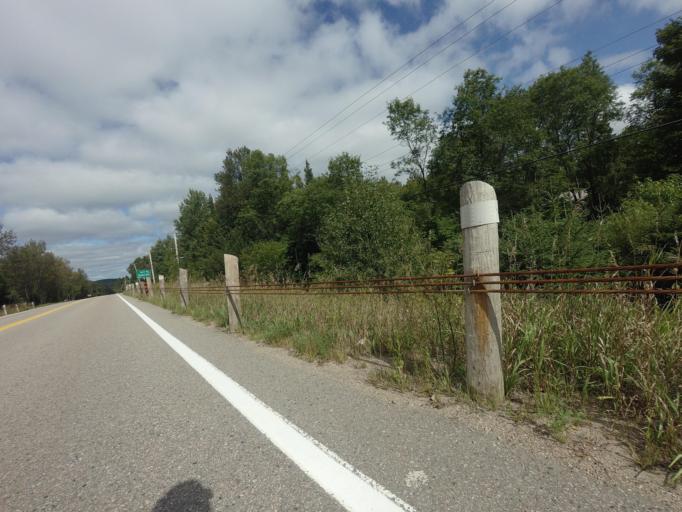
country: CA
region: Ontario
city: Bancroft
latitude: 44.9627
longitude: -78.2841
